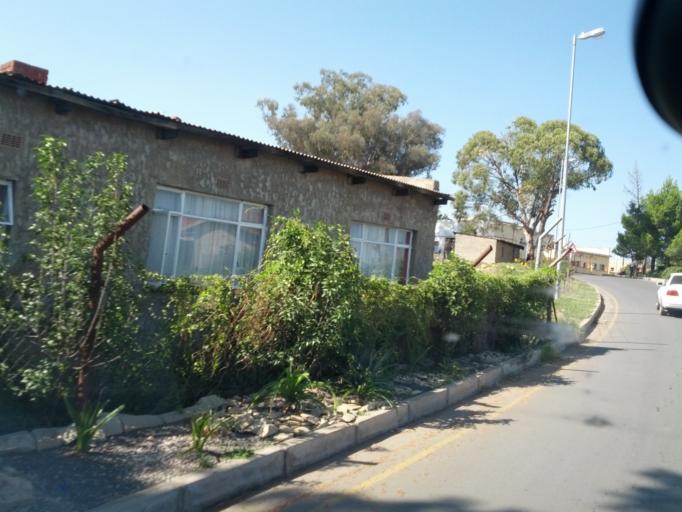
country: LS
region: Maseru
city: Maseru
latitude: -29.3048
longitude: 27.4939
